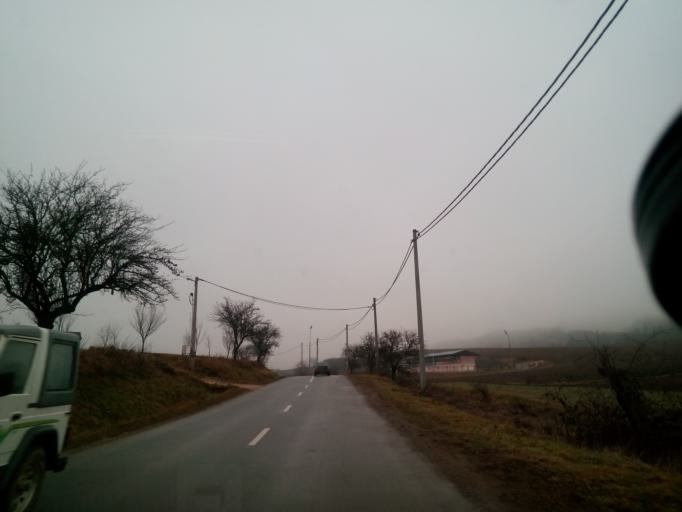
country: SK
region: Kosicky
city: Krompachy
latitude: 48.9784
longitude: 20.9461
